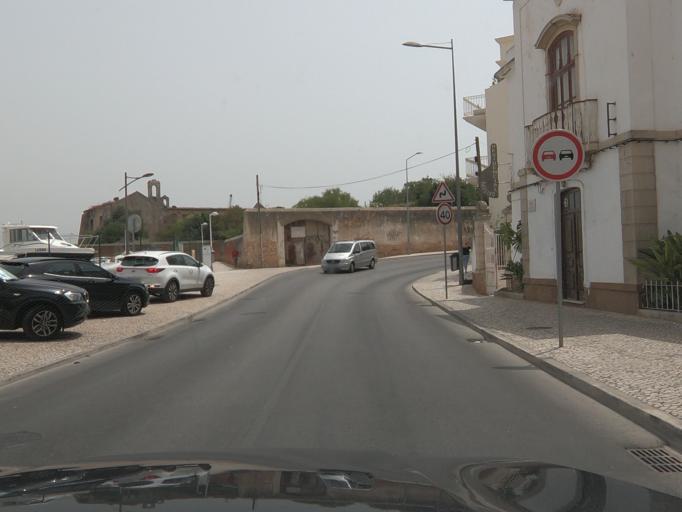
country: PT
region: Faro
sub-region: Portimao
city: Portimao
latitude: 37.1296
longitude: -8.5338
